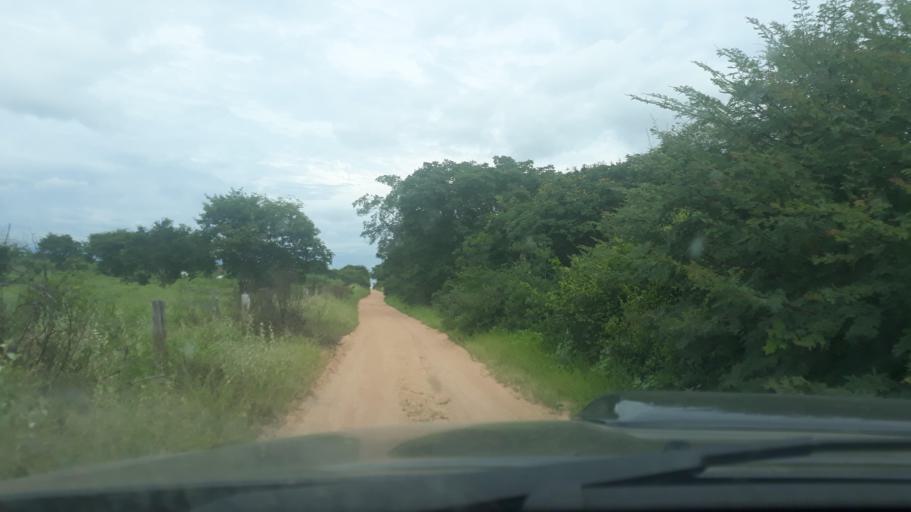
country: BR
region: Bahia
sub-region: Riacho De Santana
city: Riacho de Santana
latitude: -13.8564
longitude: -43.0461
